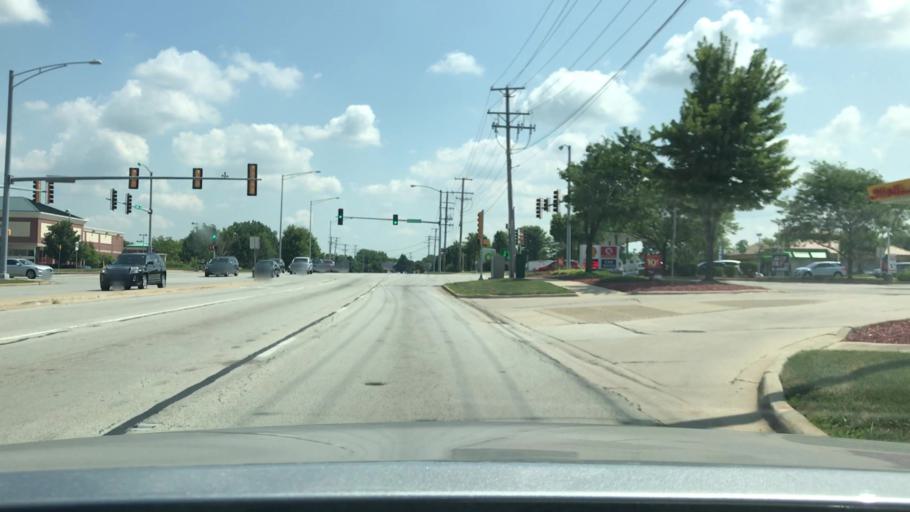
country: US
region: Illinois
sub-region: DuPage County
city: Woodridge
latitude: 41.7272
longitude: -88.0287
